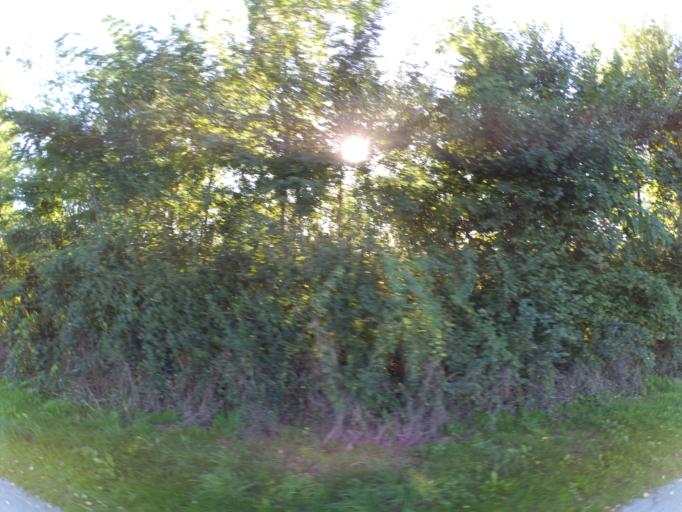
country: FR
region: Brittany
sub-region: Departement du Morbihan
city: Peillac
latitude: 47.7314
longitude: -2.2220
